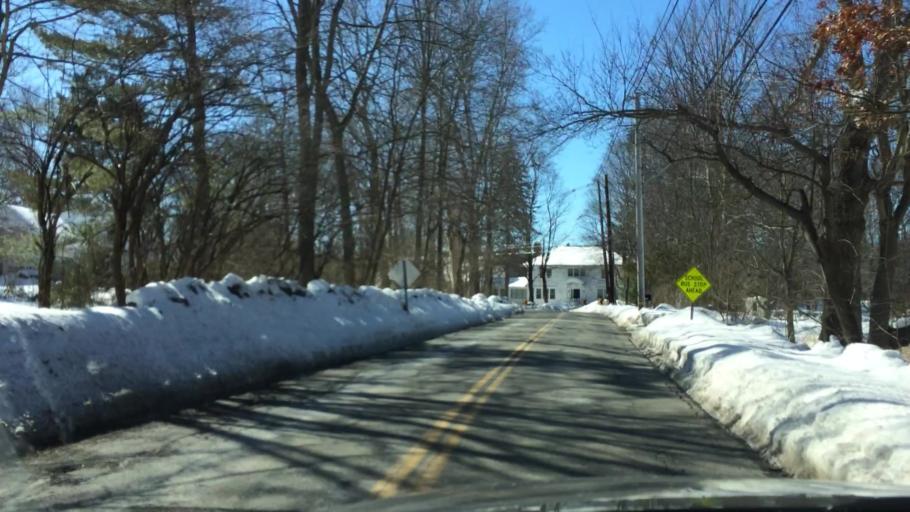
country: US
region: Massachusetts
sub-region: Middlesex County
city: Bedford
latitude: 42.5123
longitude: -71.2581
